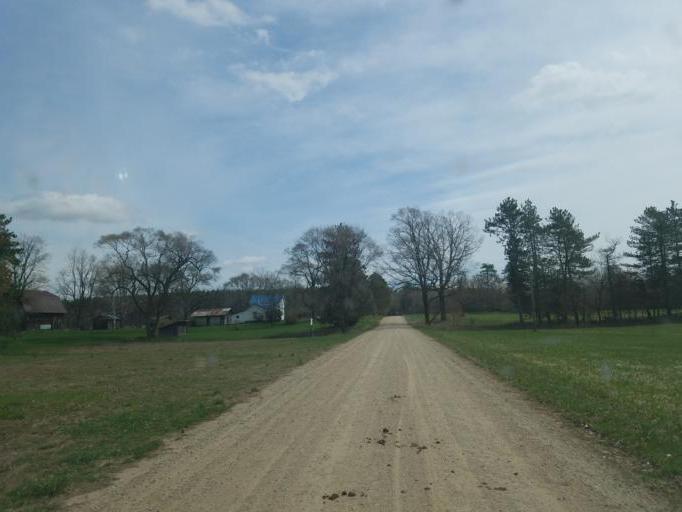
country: US
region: Michigan
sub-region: Isabella County
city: Lake Isabella
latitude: 43.5674
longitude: -84.9712
